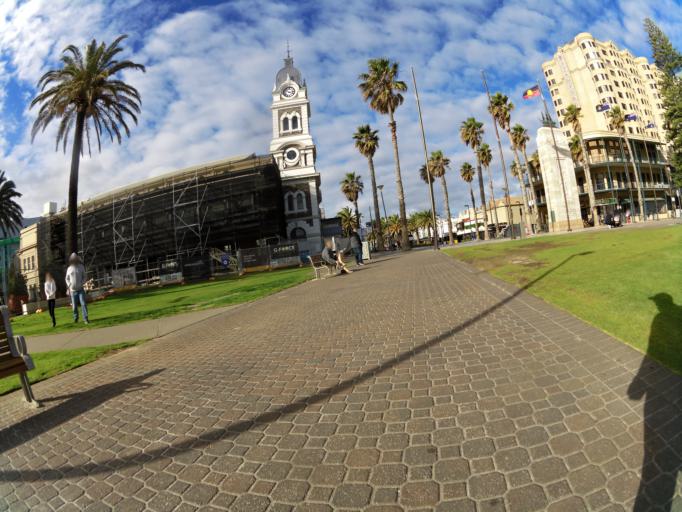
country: AU
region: South Australia
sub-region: Adelaide
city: Glenelg
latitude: -34.9802
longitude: 138.5108
